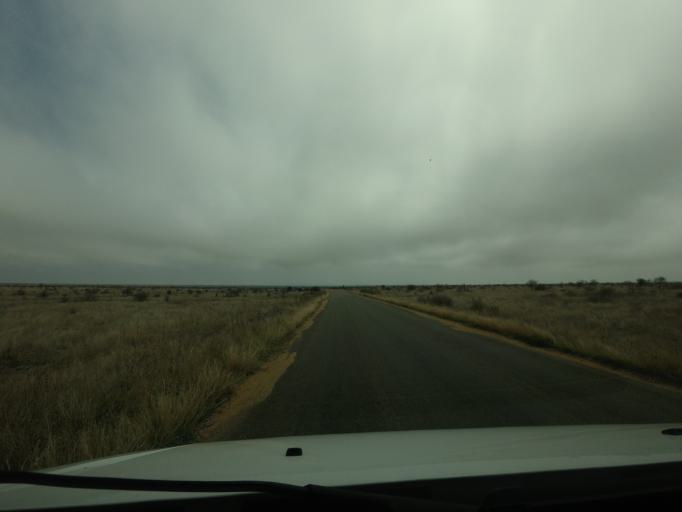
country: ZA
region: Limpopo
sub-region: Mopani District Municipality
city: Phalaborwa
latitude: -24.2151
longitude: 31.7198
